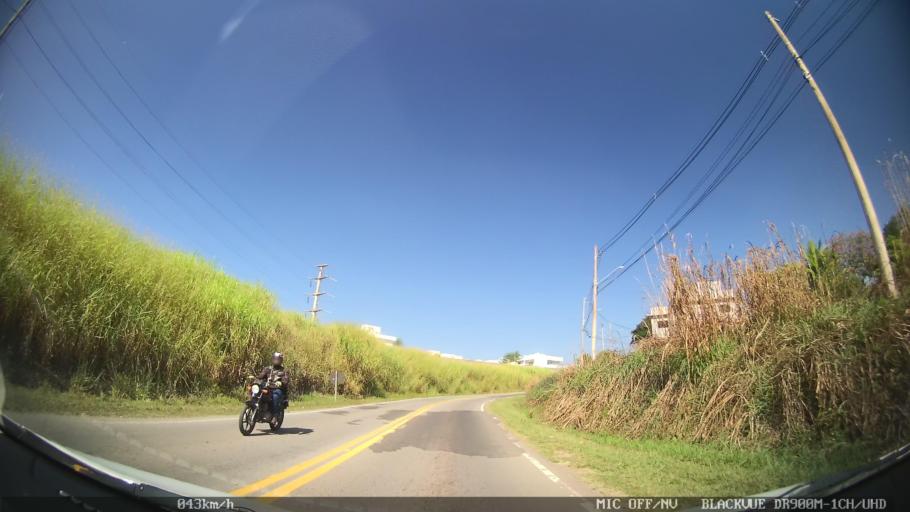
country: BR
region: Sao Paulo
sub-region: Campinas
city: Campinas
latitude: -22.9725
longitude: -47.0838
